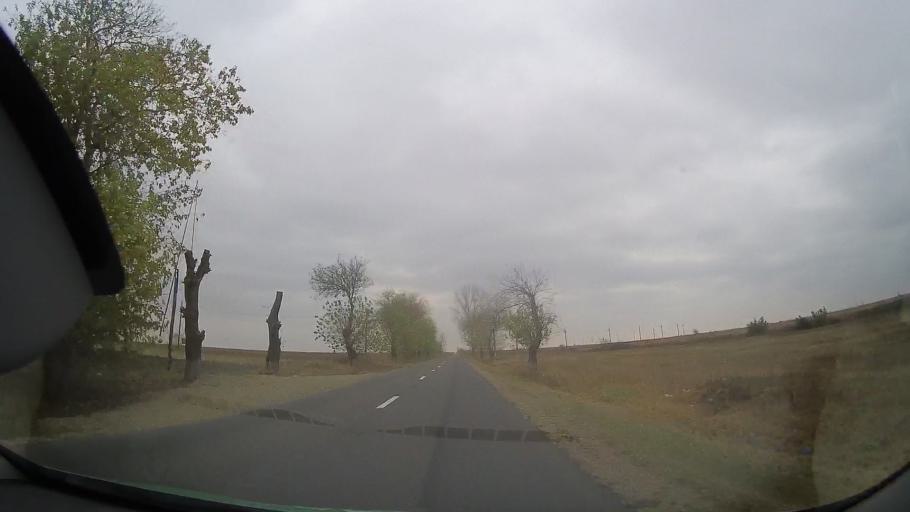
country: RO
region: Ialomita
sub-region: Comuna Garbovi
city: Garbovi
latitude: 44.7753
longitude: 26.7489
